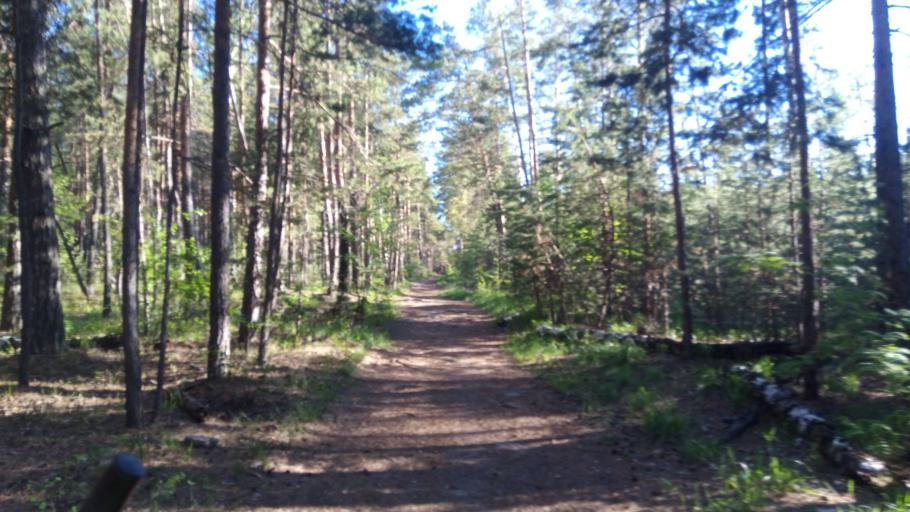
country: RU
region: Chelyabinsk
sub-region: Gorod Chelyabinsk
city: Chelyabinsk
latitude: 55.1353
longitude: 61.3357
